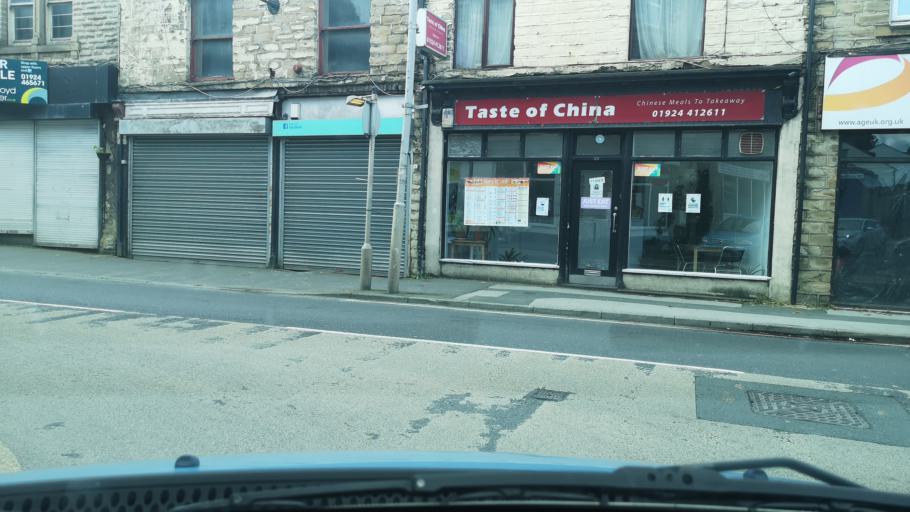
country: GB
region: England
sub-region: Kirklees
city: Heckmondwike
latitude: 53.7066
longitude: -1.6743
